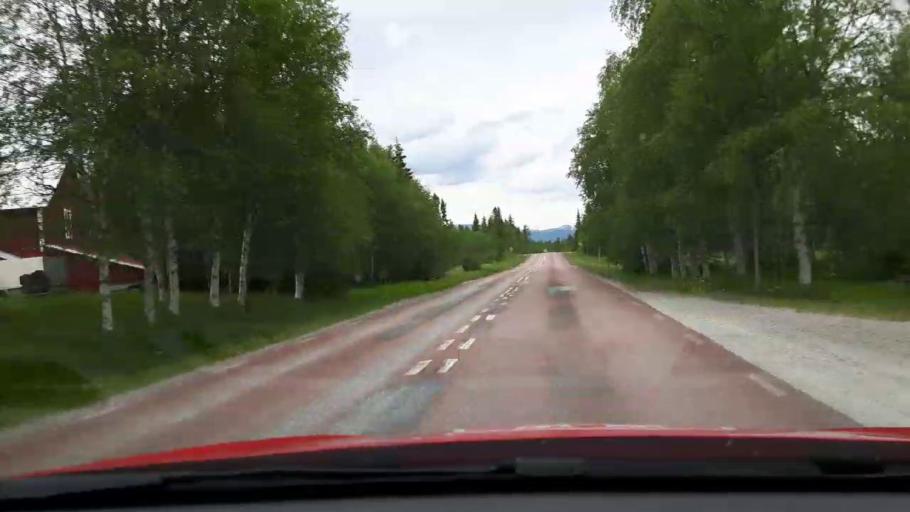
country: NO
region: Hedmark
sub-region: Engerdal
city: Engerdal
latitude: 62.5051
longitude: 12.6187
